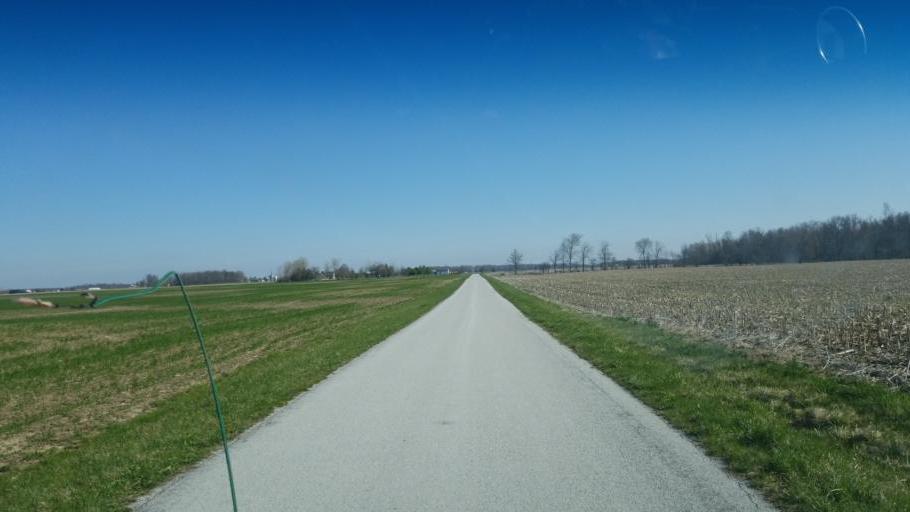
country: US
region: Ohio
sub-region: Hardin County
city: Kenton
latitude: 40.6886
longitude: -83.5593
